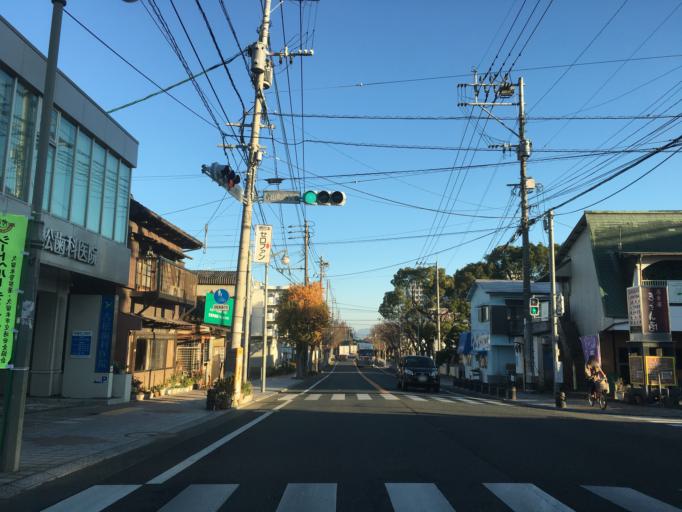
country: JP
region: Fukuoka
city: Kurume
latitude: 33.3233
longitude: 130.5090
